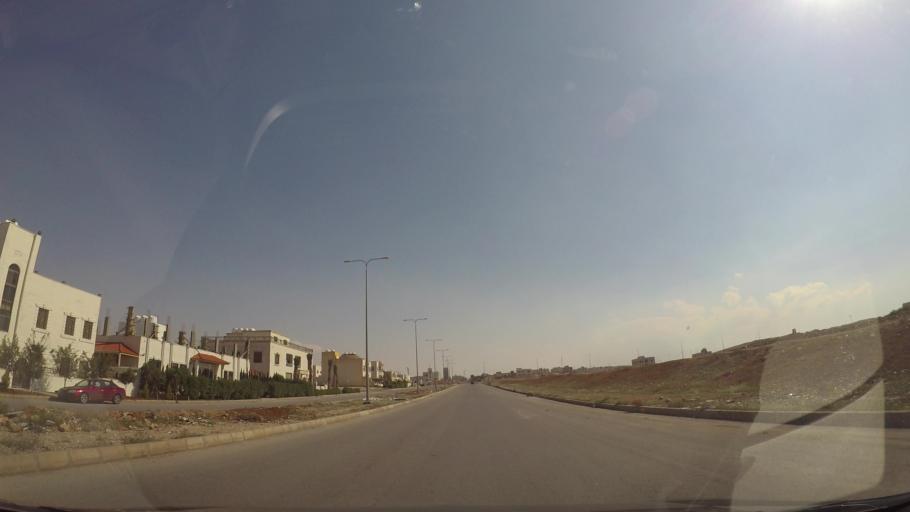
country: JO
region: Zarqa
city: Zarqa
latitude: 32.0570
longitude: 36.1144
